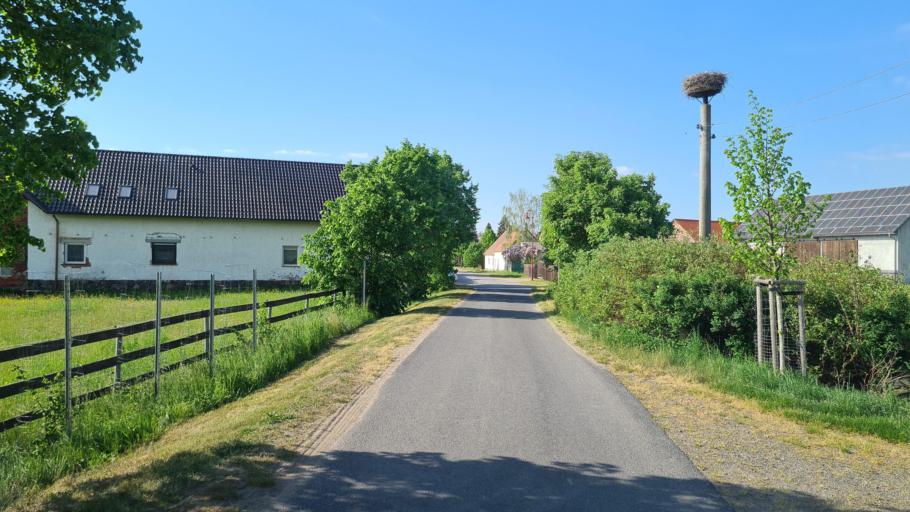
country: DE
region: Brandenburg
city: Falkenberg
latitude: 51.5886
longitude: 13.1750
